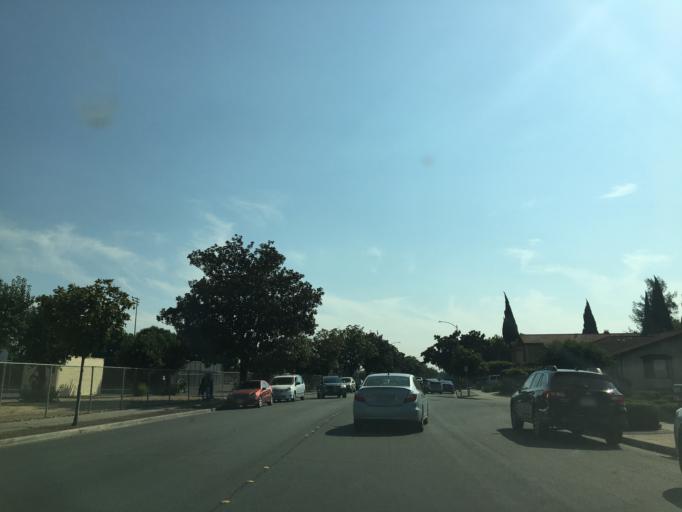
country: US
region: California
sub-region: Santa Clara County
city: Milpitas
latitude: 37.4520
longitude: -121.9050
